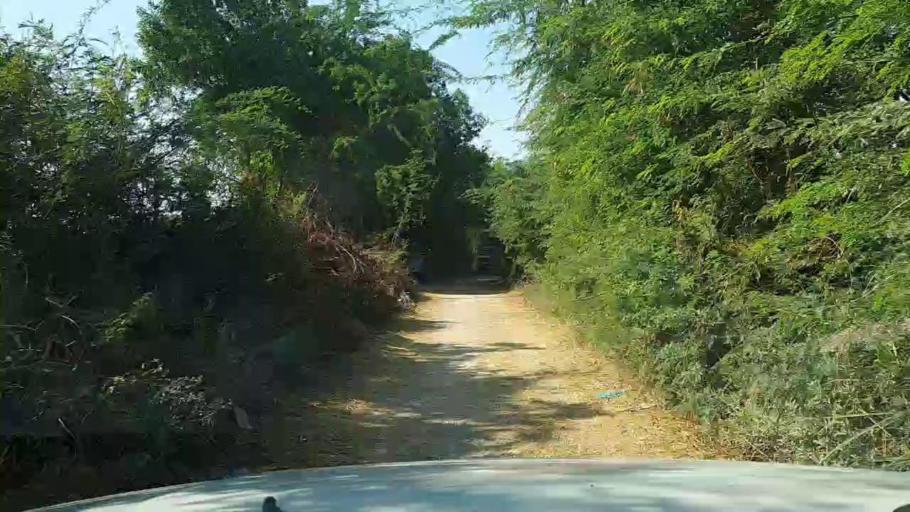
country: PK
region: Sindh
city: Mirpur Batoro
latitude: 24.6901
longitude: 68.1769
